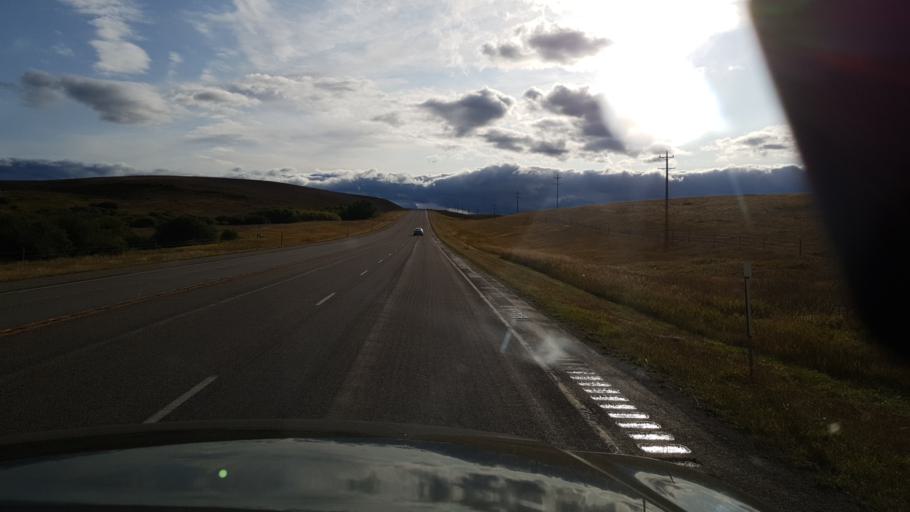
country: US
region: Montana
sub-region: Glacier County
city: South Browning
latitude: 48.5177
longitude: -113.0806
